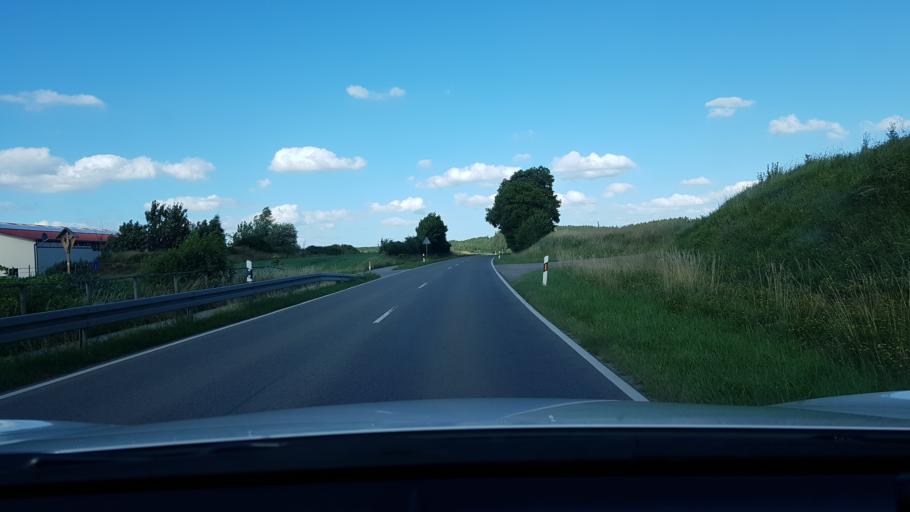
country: DE
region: Baden-Wuerttemberg
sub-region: Tuebingen Region
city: Schwendi
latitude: 48.1790
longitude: 9.9805
